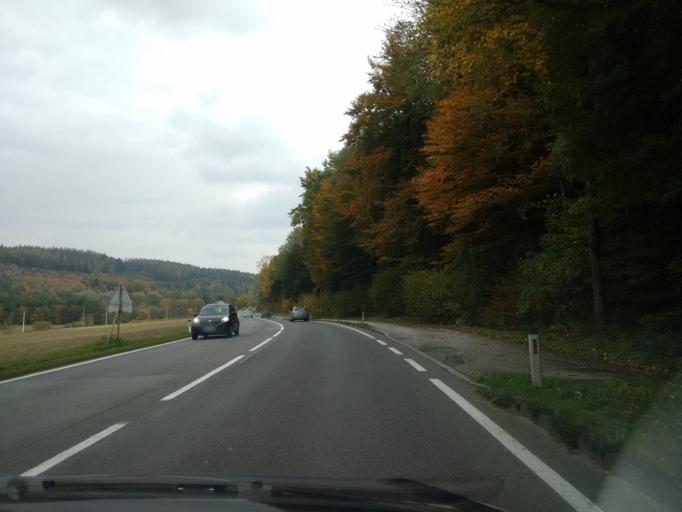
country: AT
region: Upper Austria
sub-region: Politischer Bezirk Vocklabruck
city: Attnang-Puchheim
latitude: 48.0065
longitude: 13.6881
